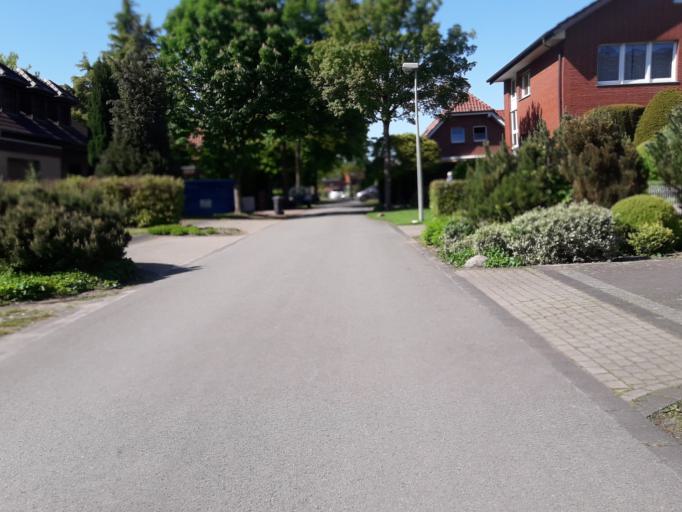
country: DE
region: North Rhine-Westphalia
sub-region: Regierungsbezirk Detmold
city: Delbruck
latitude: 51.7517
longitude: 8.5950
